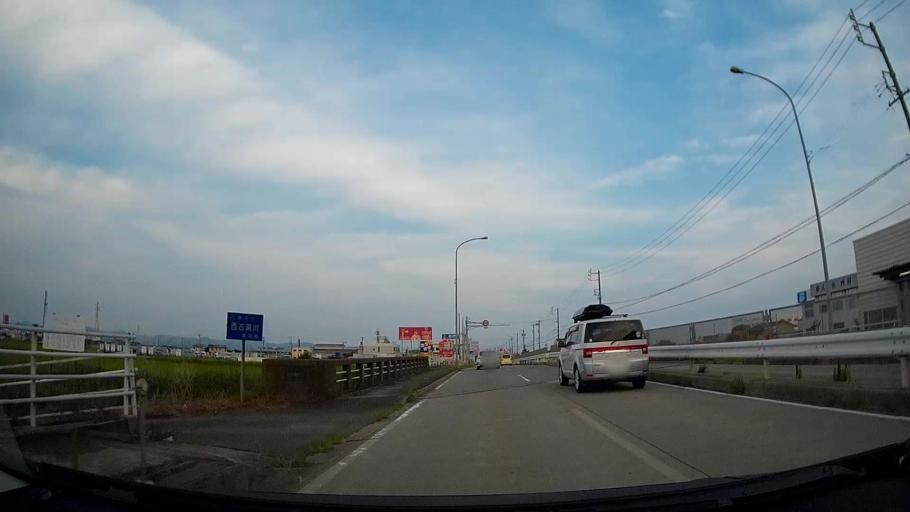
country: JP
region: Aichi
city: Kozakai-cho
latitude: 34.8237
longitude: 137.3430
